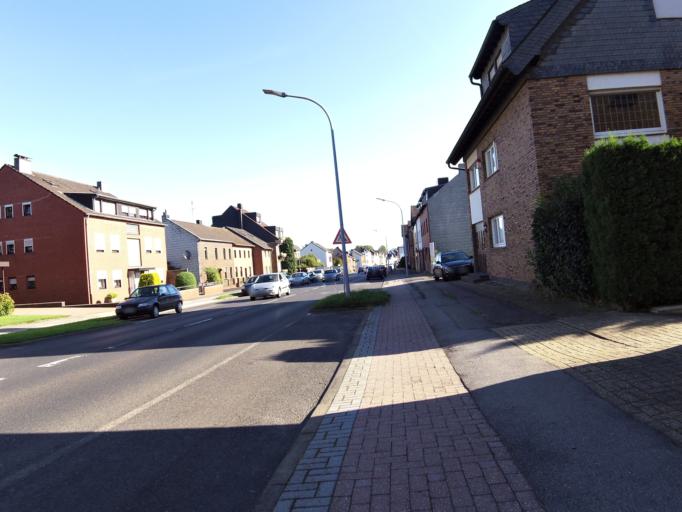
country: DE
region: North Rhine-Westphalia
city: Siersdorf
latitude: 50.8637
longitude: 6.2072
